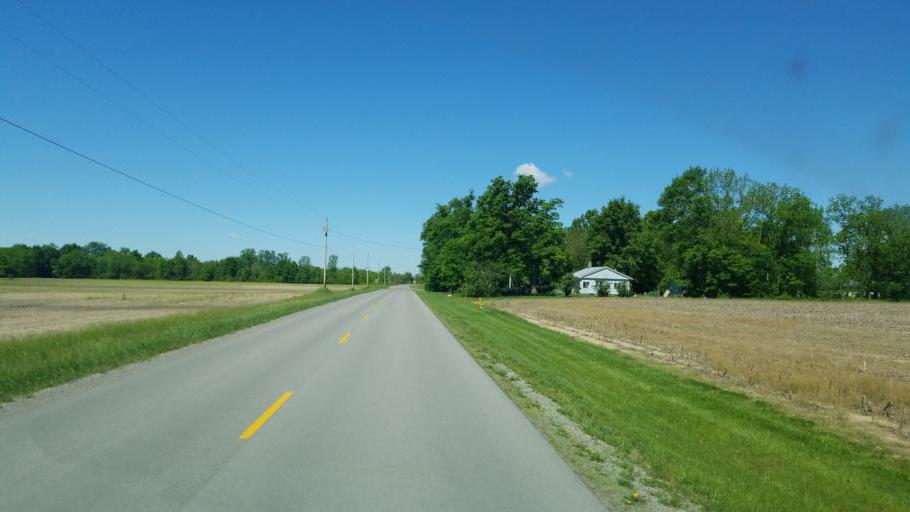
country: US
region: Ohio
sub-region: Logan County
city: Russells Point
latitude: 40.4248
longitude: -83.8483
